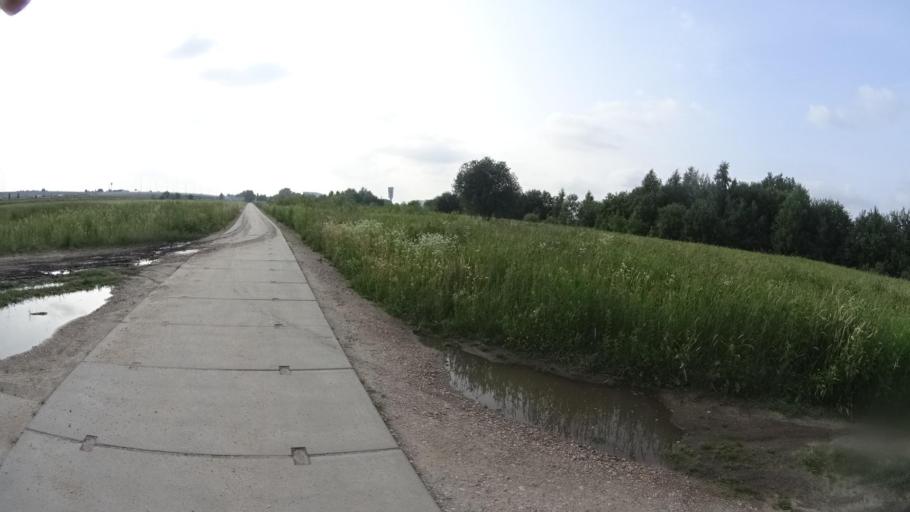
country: PL
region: Masovian Voivodeship
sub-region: Warszawa
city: Wlochy
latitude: 52.1657
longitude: 20.9451
